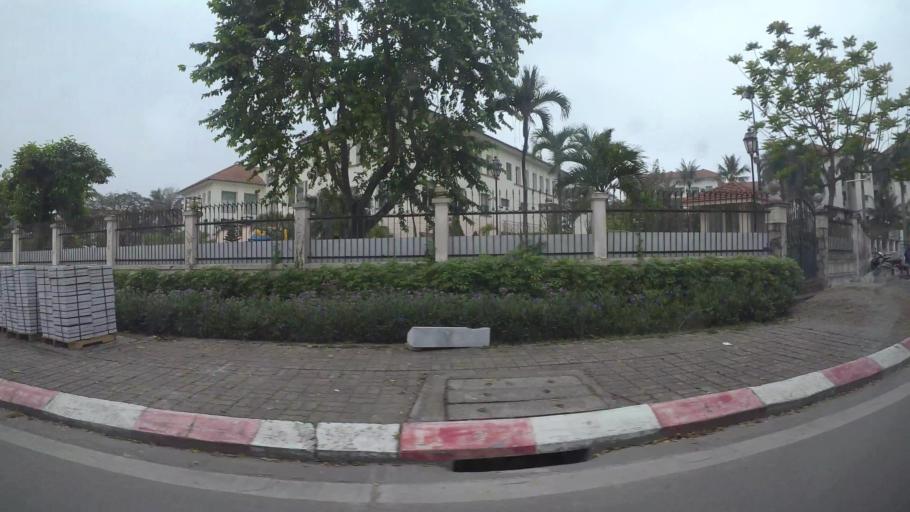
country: VN
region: Ha Noi
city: Tay Ho
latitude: 21.0661
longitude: 105.8195
